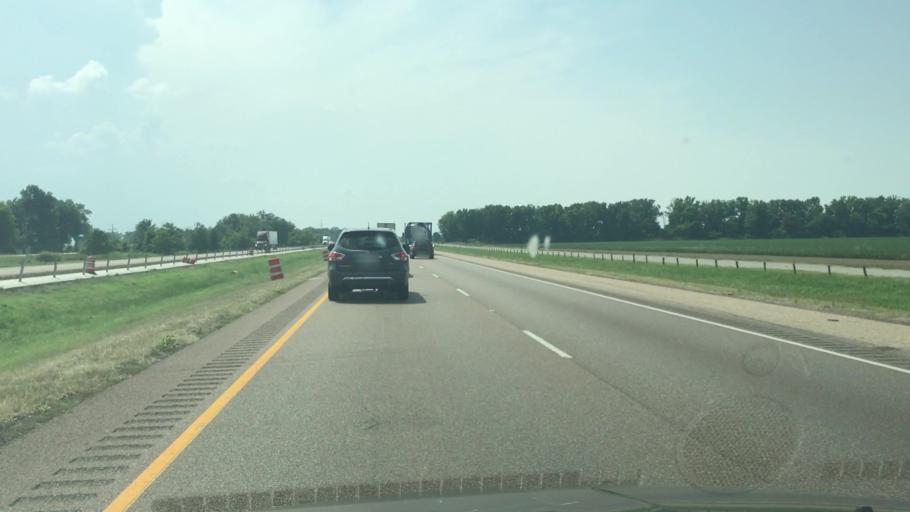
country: US
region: Arkansas
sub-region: Crittenden County
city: West Memphis
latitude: 35.1485
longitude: -90.3324
